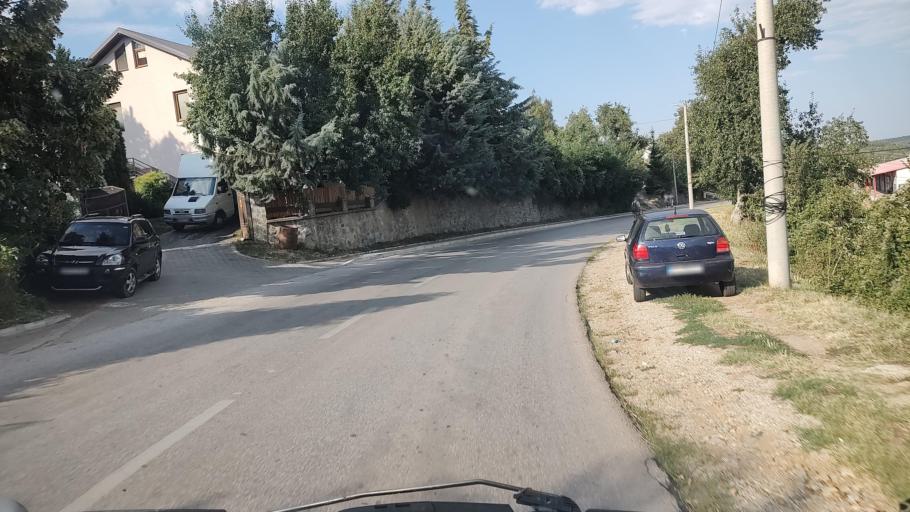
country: MK
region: Kriva Palanka
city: Kriva Palanka
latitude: 42.1927
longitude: 22.3129
